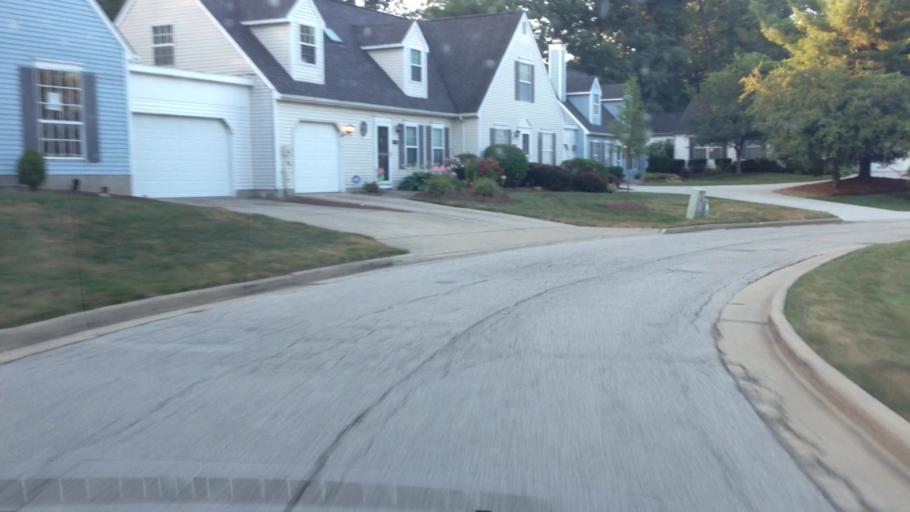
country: US
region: Ohio
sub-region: Summit County
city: Cuyahoga Falls
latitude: 41.1606
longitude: -81.4993
